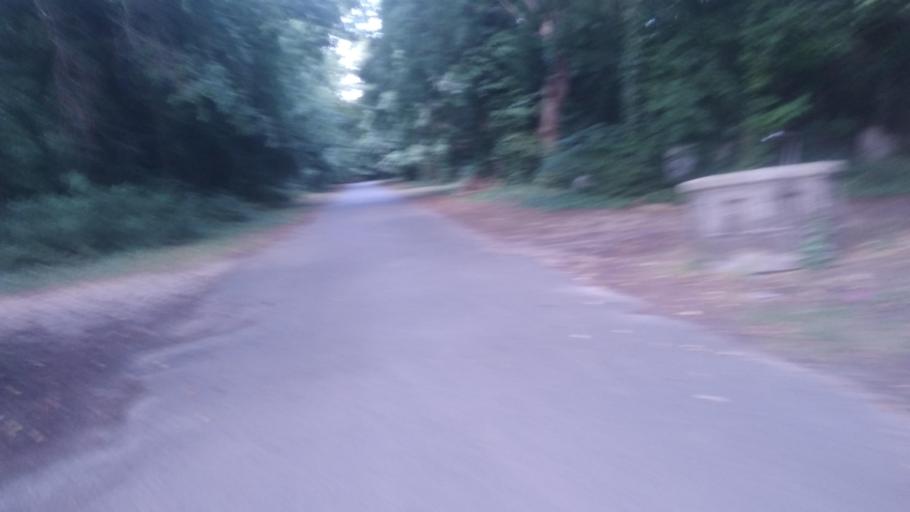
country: HU
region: Budapest
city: Budapest XVIII. keruelet
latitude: 47.4746
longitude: 19.1937
